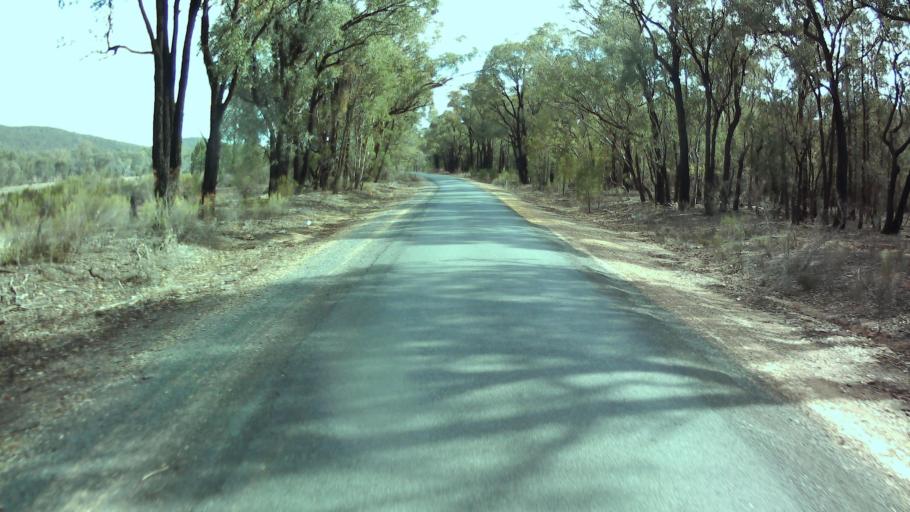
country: AU
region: New South Wales
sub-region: Weddin
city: Grenfell
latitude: -33.8604
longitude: 148.2145
